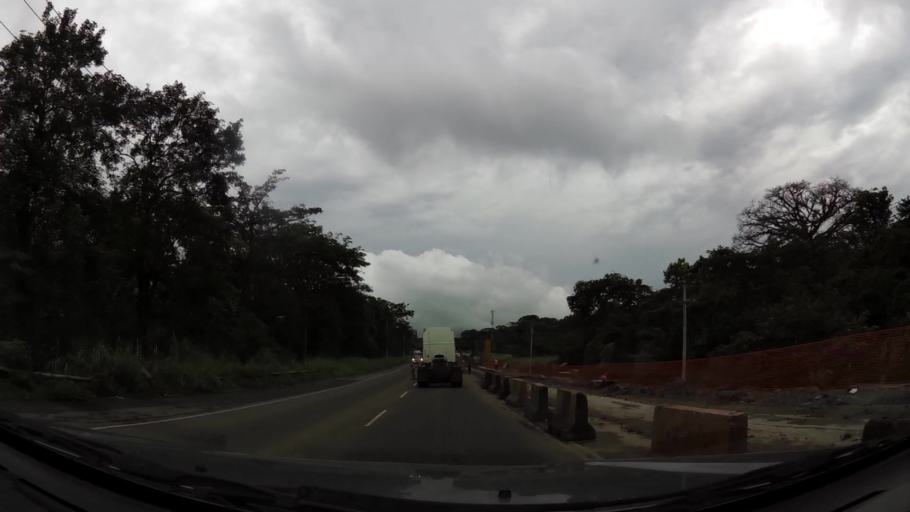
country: PA
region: Colon
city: Nuevo Vigia
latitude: 9.2114
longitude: -79.6260
